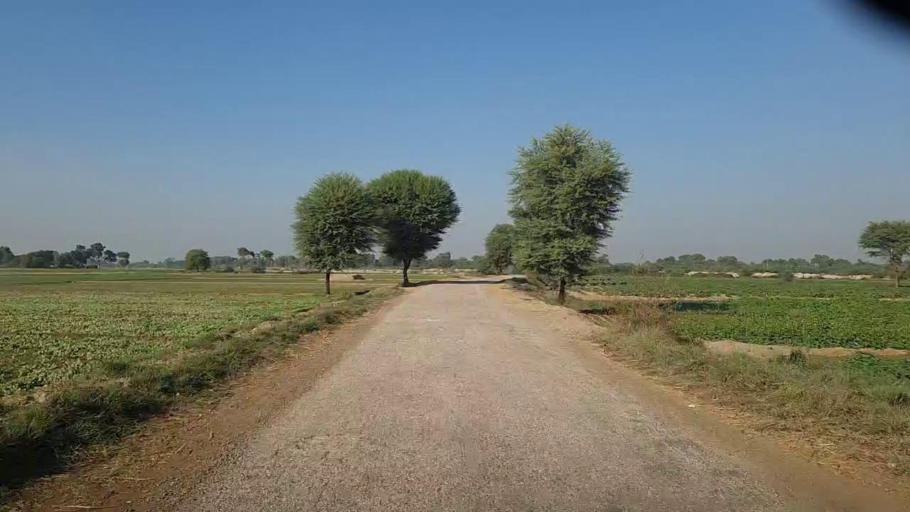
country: PK
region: Sindh
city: Darya Khan Marri
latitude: 26.6870
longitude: 68.3513
